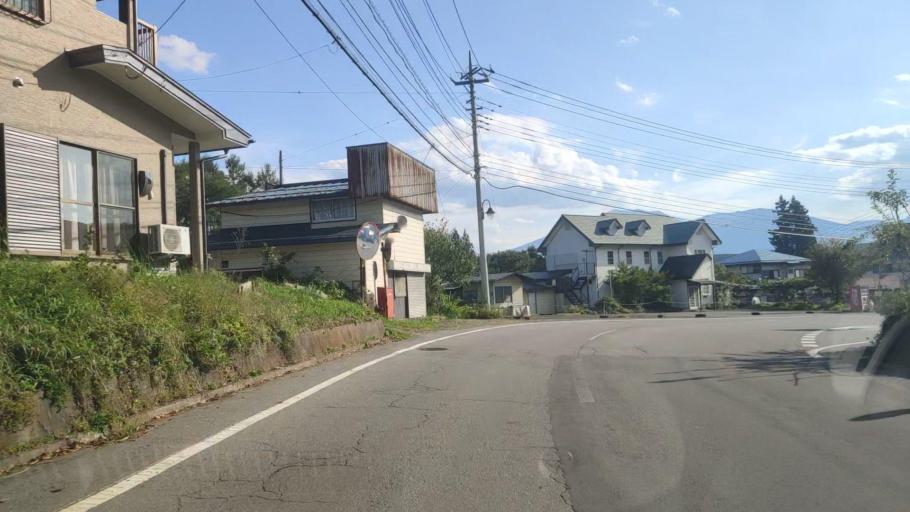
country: JP
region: Nagano
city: Komoro
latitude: 36.5429
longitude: 138.5567
